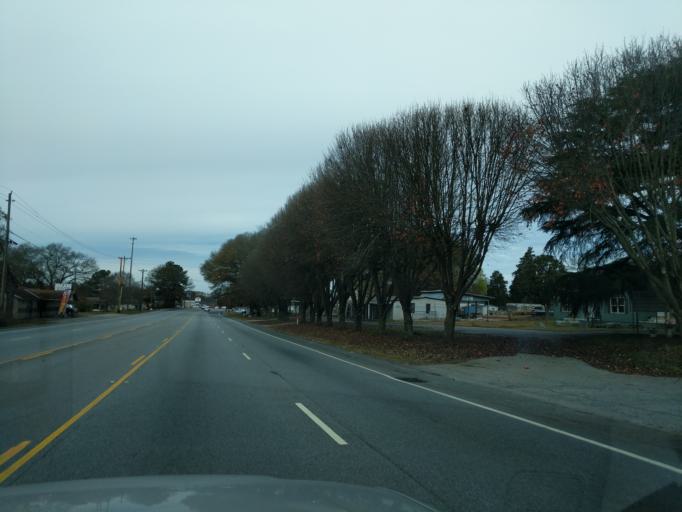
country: US
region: South Carolina
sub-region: Anderson County
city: Pendleton
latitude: 34.5965
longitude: -82.7510
